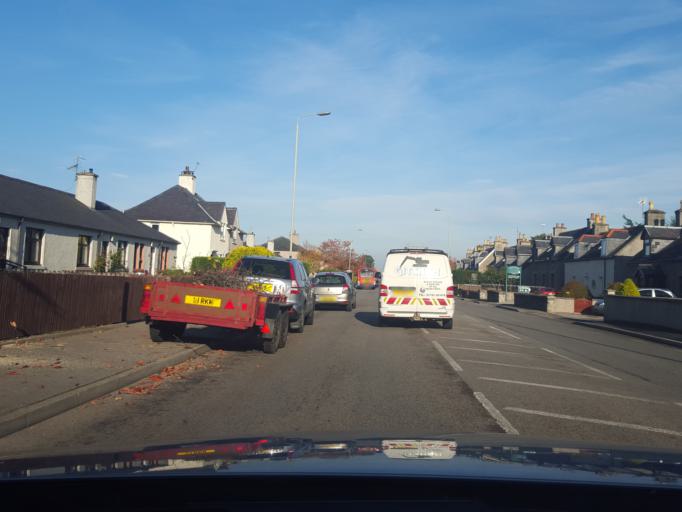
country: GB
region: Scotland
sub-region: Highland
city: Inverness
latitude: 57.4683
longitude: -4.2384
